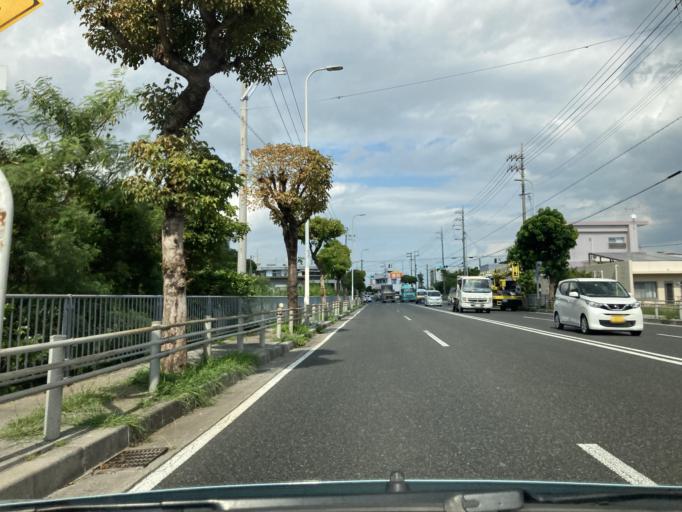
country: JP
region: Okinawa
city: Ginowan
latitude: 26.2439
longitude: 127.7804
